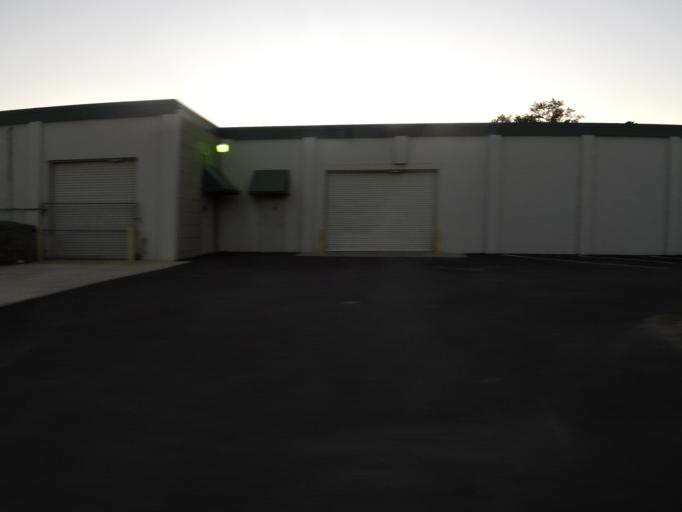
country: US
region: Florida
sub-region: Duval County
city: Jacksonville
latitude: 30.2711
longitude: -81.6306
